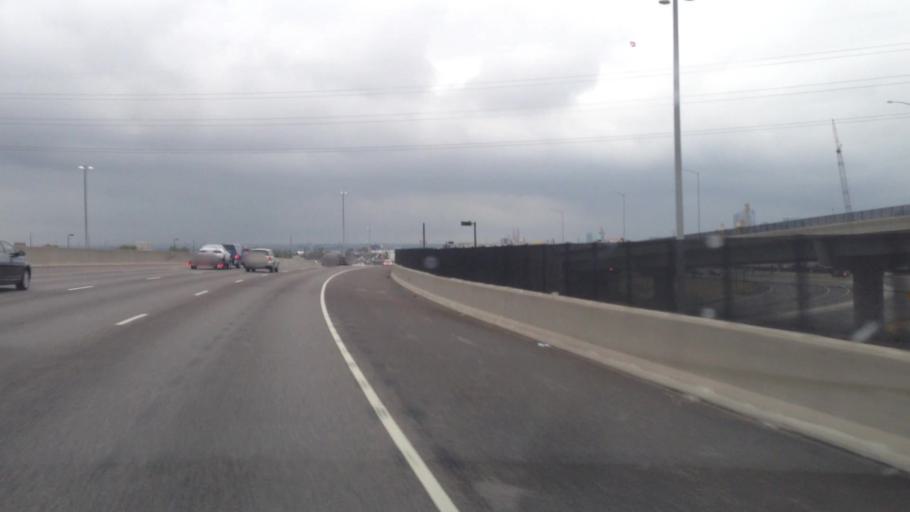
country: US
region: Colorado
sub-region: Denver County
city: Denver
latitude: 39.7062
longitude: -104.9962
